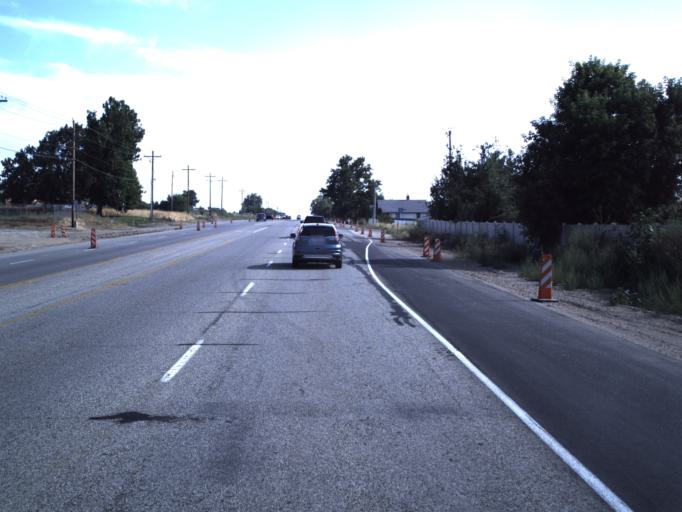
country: US
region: Utah
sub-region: Box Elder County
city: South Willard
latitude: 41.3668
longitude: -112.0355
